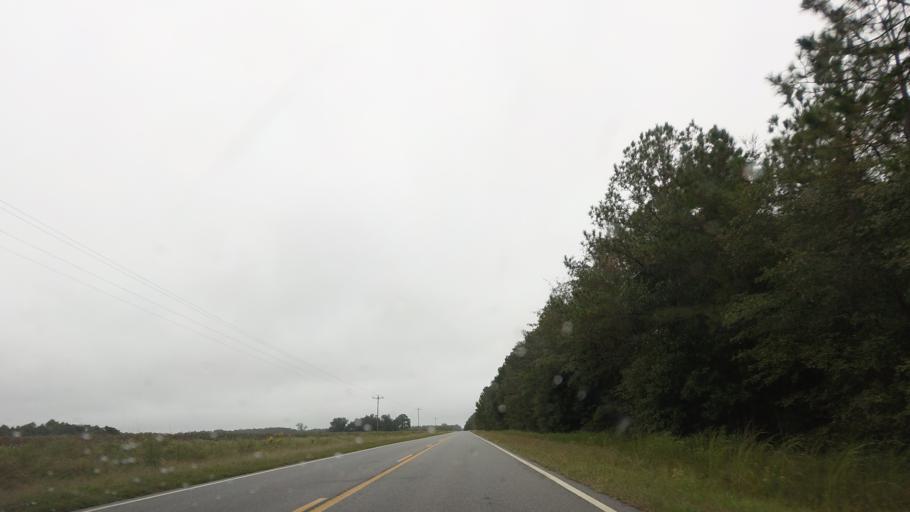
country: US
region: Georgia
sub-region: Berrien County
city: Enigma
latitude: 31.4588
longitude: -83.2384
